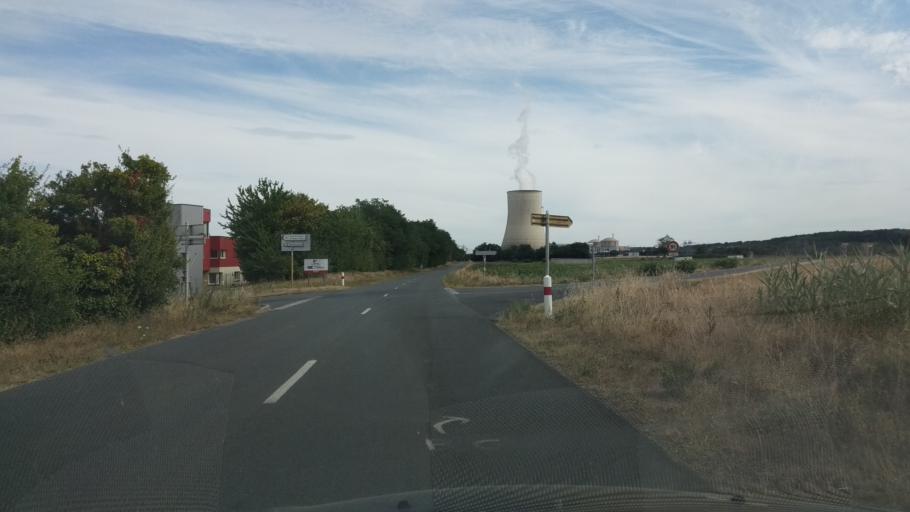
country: FR
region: Poitou-Charentes
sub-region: Departement de la Vienne
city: Terce
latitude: 46.4745
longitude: 0.6463
